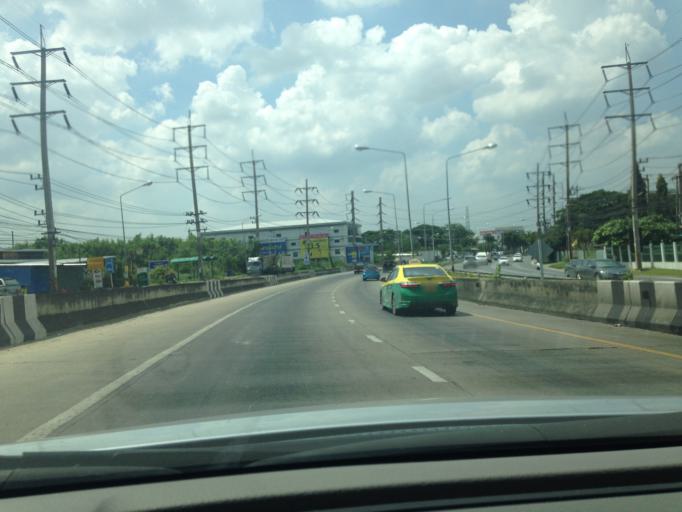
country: TH
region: Phra Nakhon Si Ayutthaya
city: Ban Bang Kadi Pathum Thani
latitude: 13.9842
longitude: 100.5907
